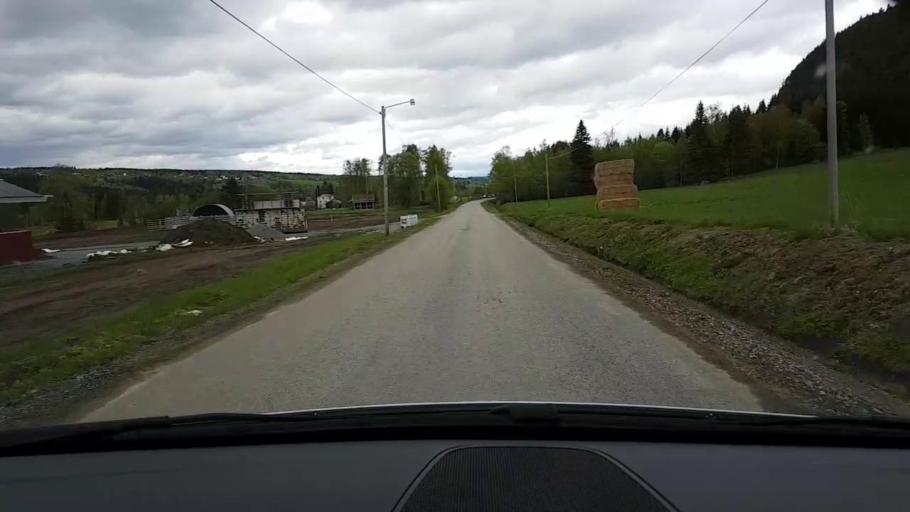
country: SE
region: Jaemtland
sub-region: Bergs Kommun
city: Hoverberg
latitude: 62.8258
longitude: 14.4219
